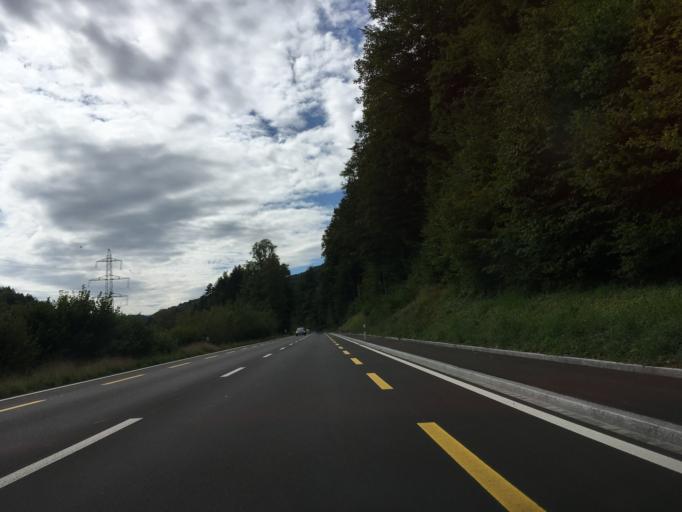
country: CH
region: Zurich
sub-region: Bezirk Horgen
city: Oberrieden / Berg
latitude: 47.2644
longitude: 8.5590
